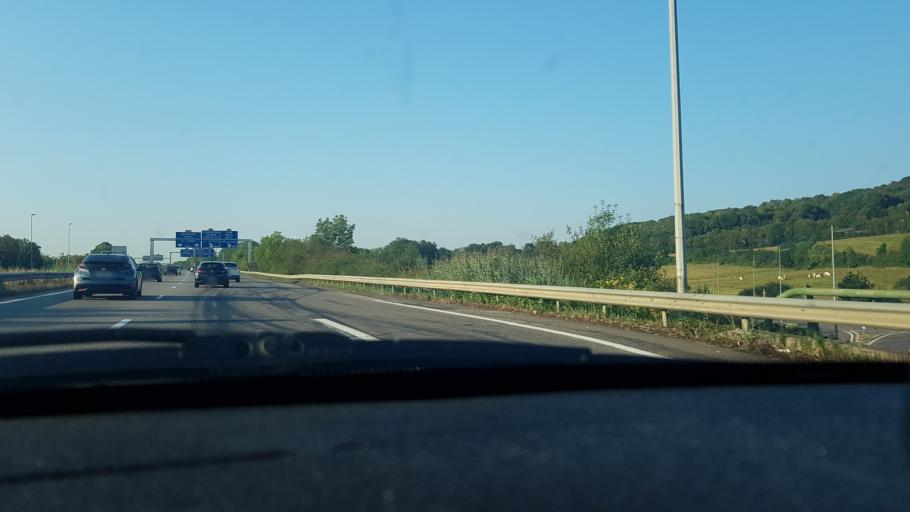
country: FR
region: Lorraine
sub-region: Departement de Meurthe-et-Moselle
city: Vandoeuvre-les-Nancy
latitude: 48.6352
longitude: 6.1817
